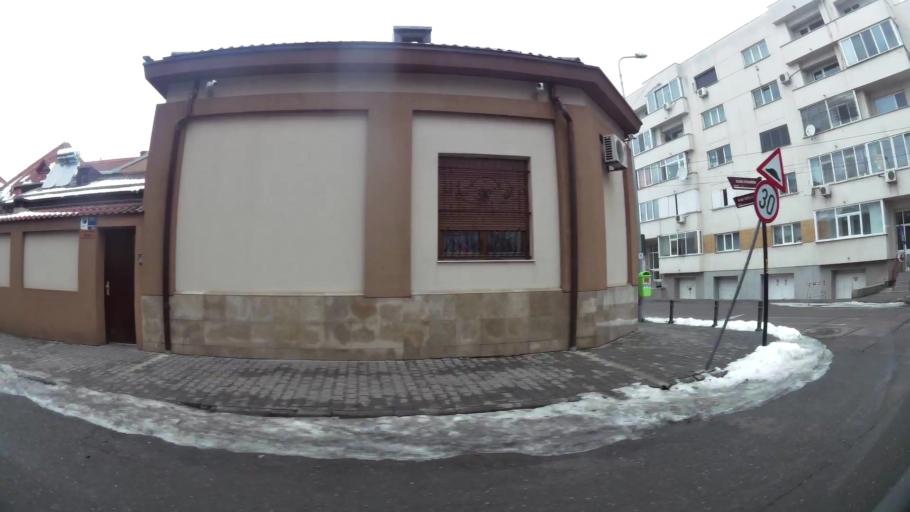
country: RO
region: Bucuresti
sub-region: Municipiul Bucuresti
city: Bucharest
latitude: 44.4299
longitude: 26.1237
